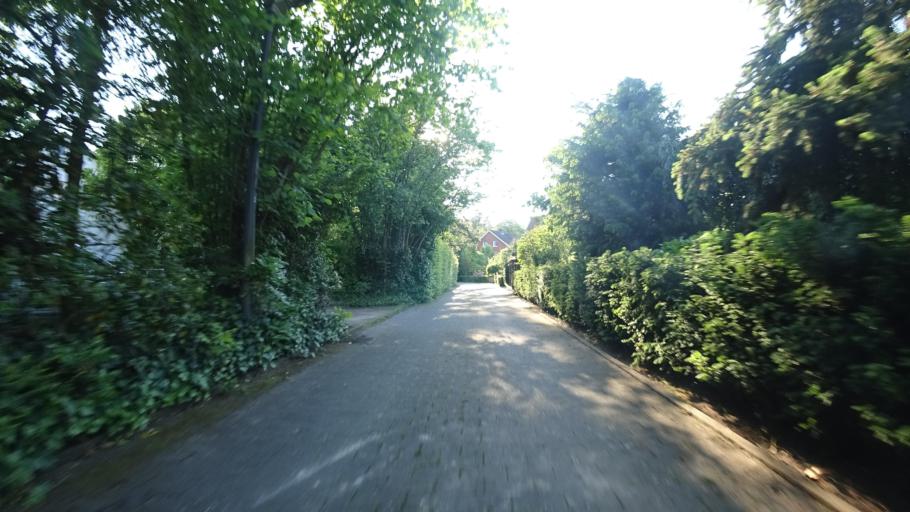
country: DE
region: North Rhine-Westphalia
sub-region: Regierungsbezirk Detmold
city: Guetersloh
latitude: 51.9478
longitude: 8.4077
